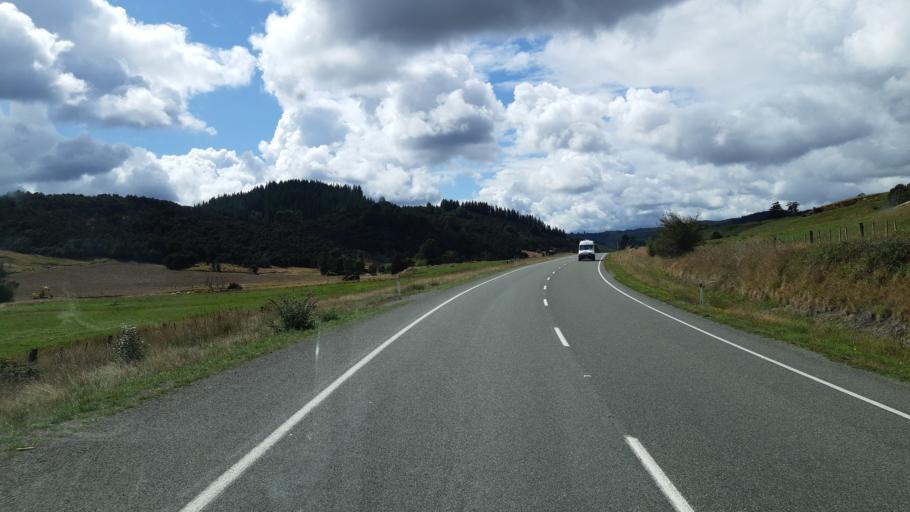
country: NZ
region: Tasman
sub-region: Tasman District
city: Wakefield
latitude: -41.6423
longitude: 172.6612
